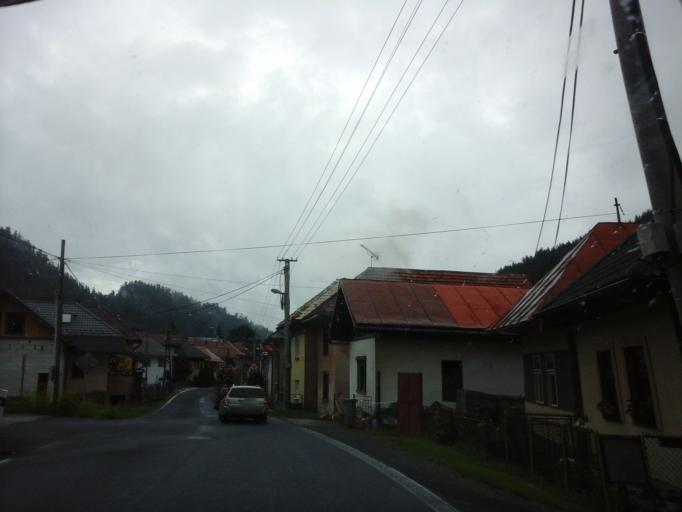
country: SK
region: Kosicky
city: Dobsina
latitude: 48.9181
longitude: 20.2712
